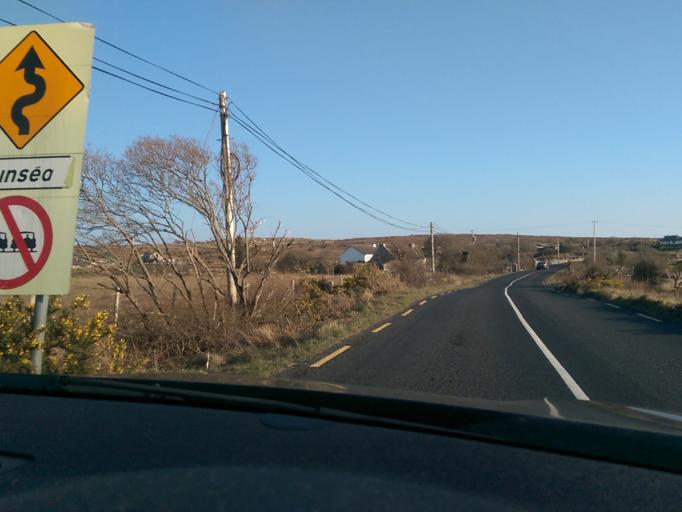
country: IE
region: Connaught
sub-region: County Galway
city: Oughterard
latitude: 53.3244
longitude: -9.5462
